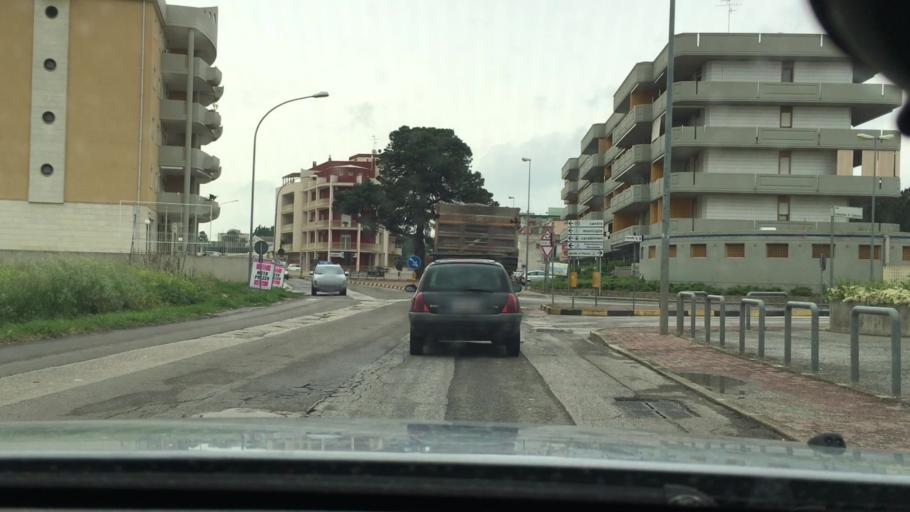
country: IT
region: Apulia
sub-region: Provincia di Bari
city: Gioia del Colle
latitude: 40.8076
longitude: 16.9245
